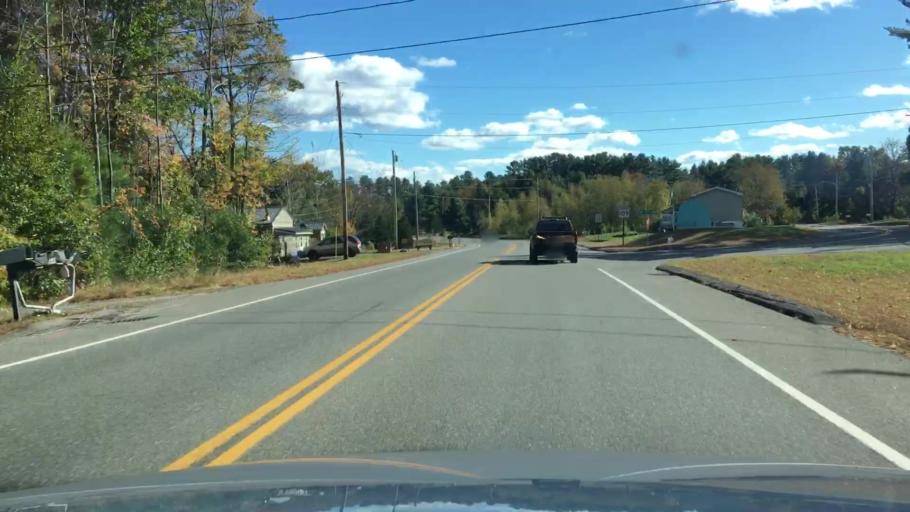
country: US
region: Maine
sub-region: York County
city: South Sanford
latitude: 43.3650
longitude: -70.6694
